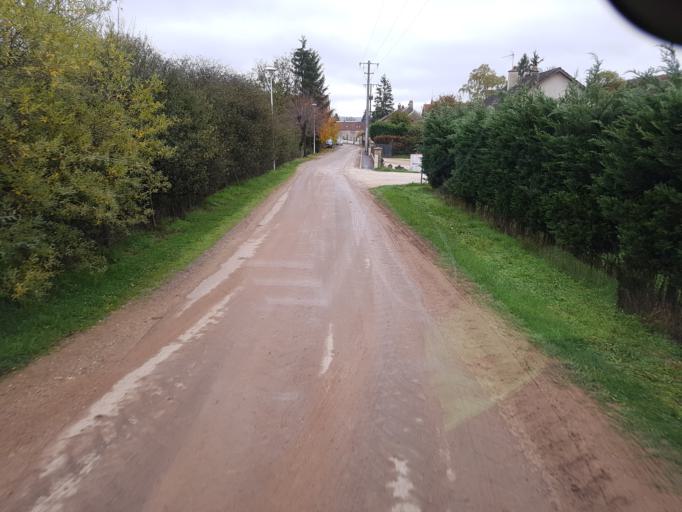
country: FR
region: Bourgogne
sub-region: Departement de la Cote-d'Or
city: Is-sur-Tille
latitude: 47.5348
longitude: 4.9815
